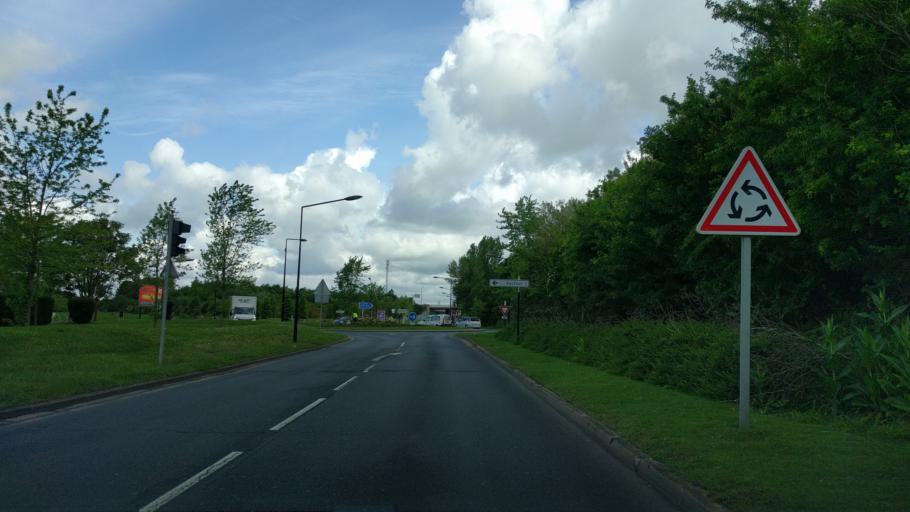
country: FR
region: Ile-de-France
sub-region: Departement de Seine-et-Marne
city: Nandy
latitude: 48.6049
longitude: 2.5792
